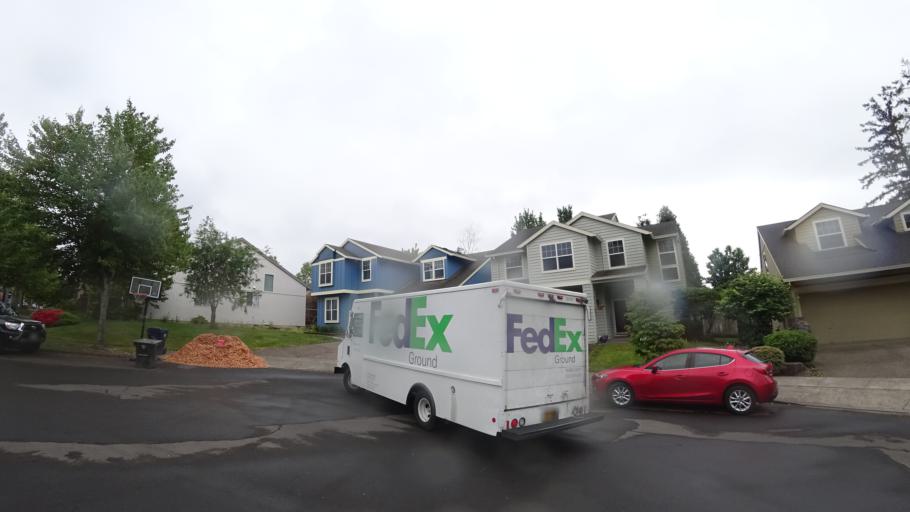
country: US
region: Oregon
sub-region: Washington County
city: Rockcreek
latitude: 45.5309
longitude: -122.8928
